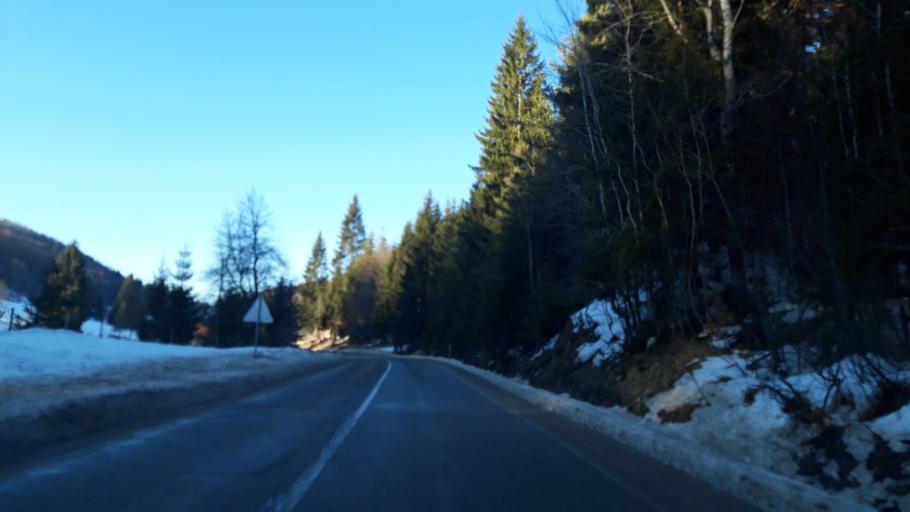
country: BA
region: Republika Srpska
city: Han Pijesak
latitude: 44.1236
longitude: 18.9647
